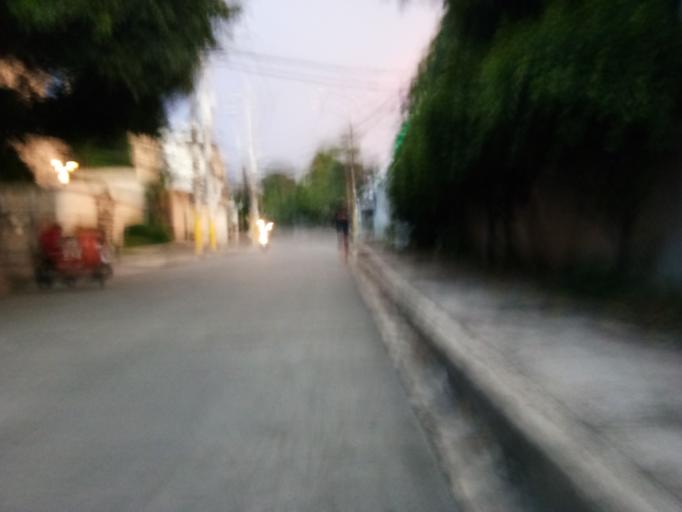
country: PH
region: Metro Manila
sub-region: San Juan
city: San Juan
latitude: 14.6120
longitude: 121.0484
